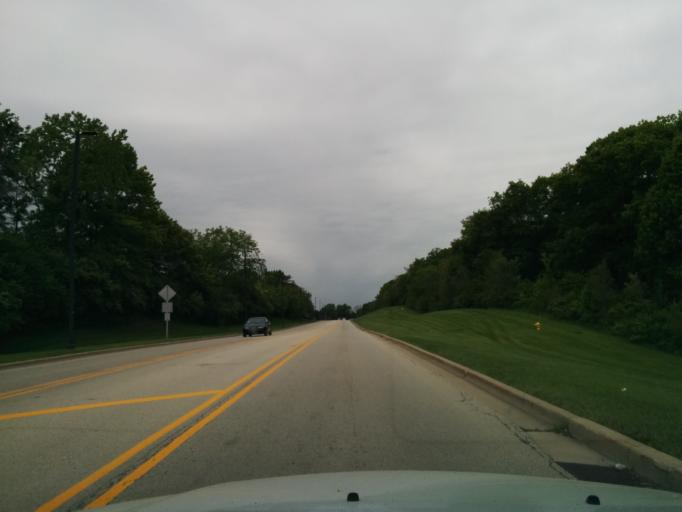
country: US
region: Illinois
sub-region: Cook County
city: Willow Springs
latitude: 41.7536
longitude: -87.8810
